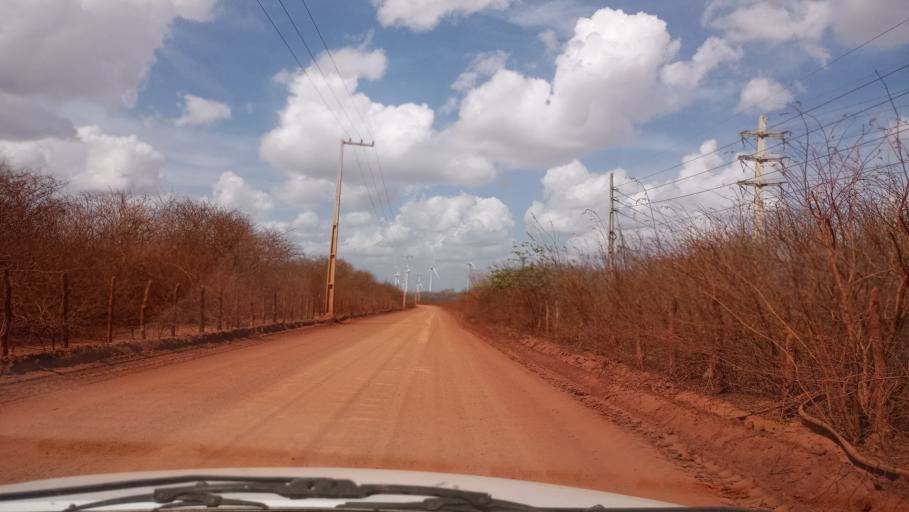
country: BR
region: Rio Grande do Norte
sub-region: Joao Camara
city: Joao Camara
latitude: -5.3642
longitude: -35.8373
